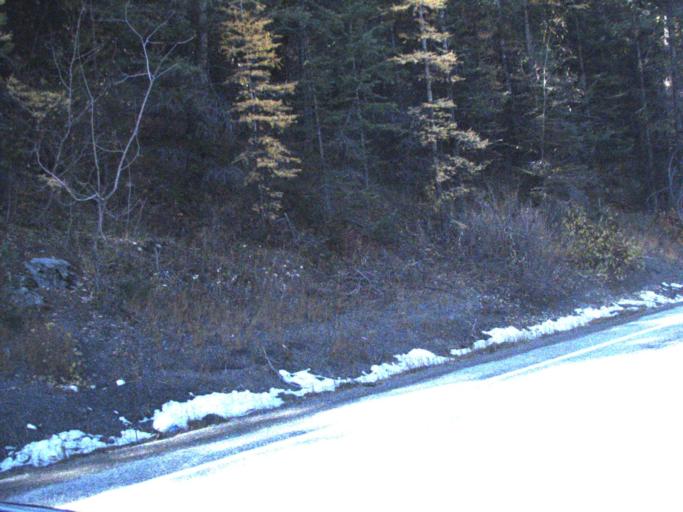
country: US
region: Washington
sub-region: Ferry County
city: Republic
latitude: 48.6138
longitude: -118.4442
